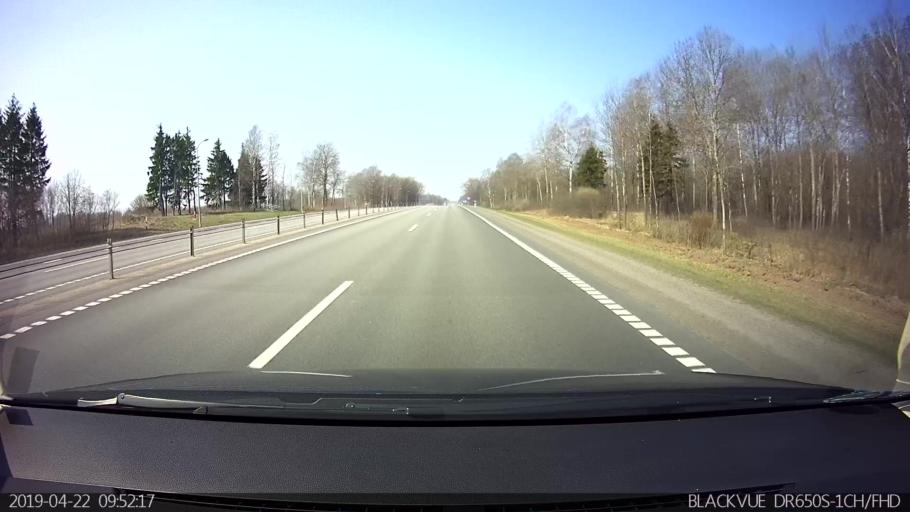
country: BY
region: Vitebsk
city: Dubrowna
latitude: 54.6859
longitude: 30.8256
